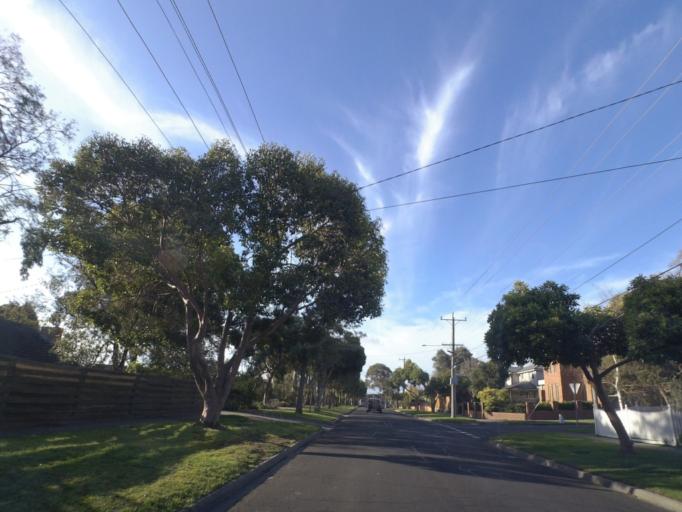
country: AU
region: Victoria
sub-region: Whitehorse
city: Box Hill North
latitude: -37.8006
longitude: 145.1341
